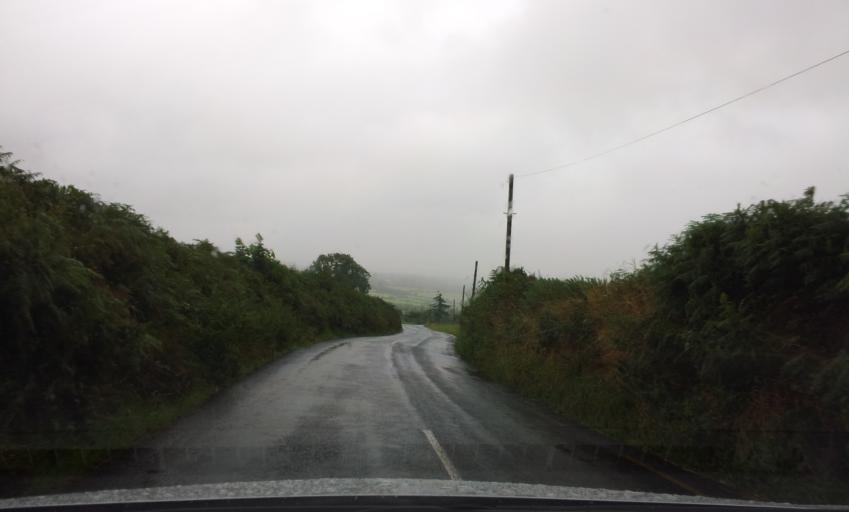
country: IE
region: Leinster
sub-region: Loch Garman
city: New Ross
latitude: 52.4085
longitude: -7.0323
